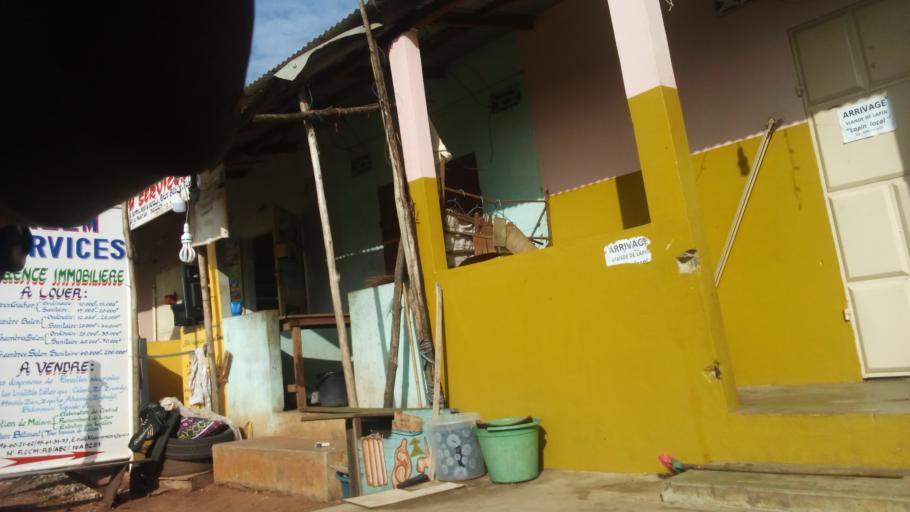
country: BJ
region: Atlantique
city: Abomey-Calavi
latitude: 6.4309
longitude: 2.3411
